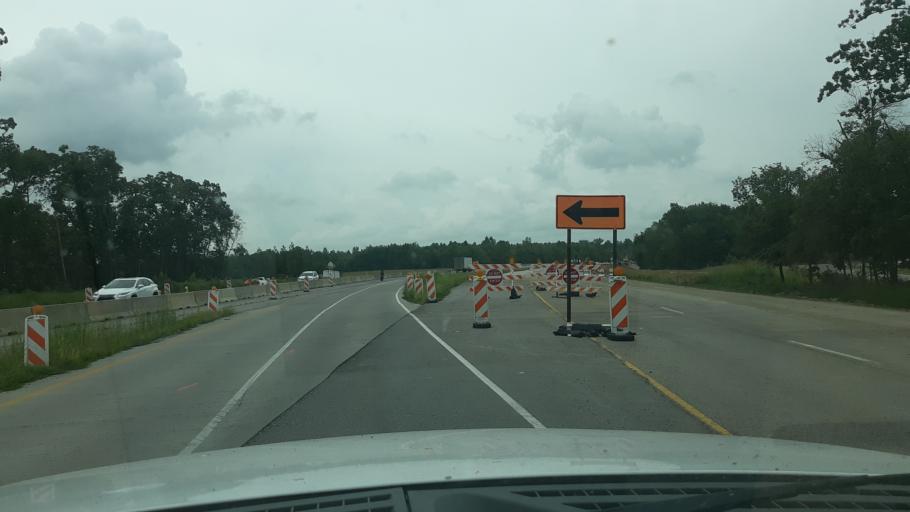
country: US
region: Illinois
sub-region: Jackson County
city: Carbondale
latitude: 37.7366
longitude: -89.1843
